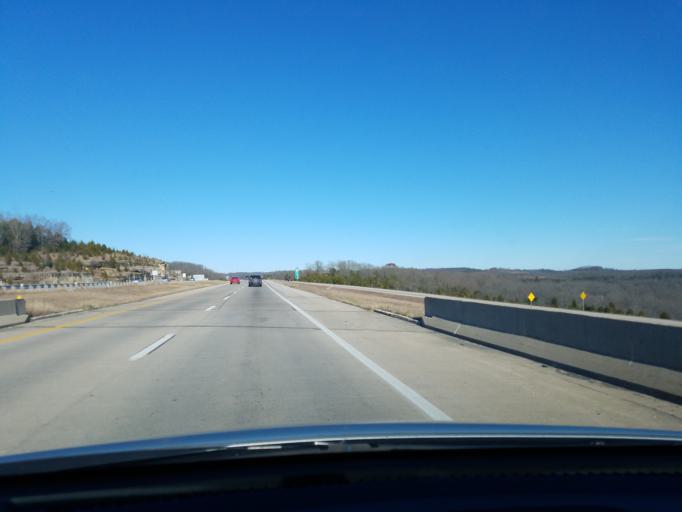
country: US
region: Missouri
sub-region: Taney County
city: Merriam Woods
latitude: 36.7493
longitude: -93.2227
